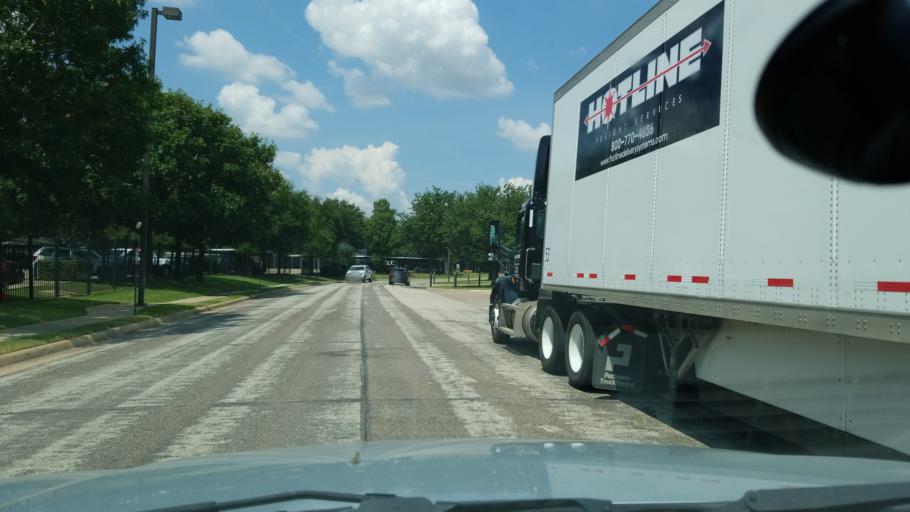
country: US
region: Texas
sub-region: Dallas County
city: Farmers Branch
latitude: 32.8595
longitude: -96.8993
